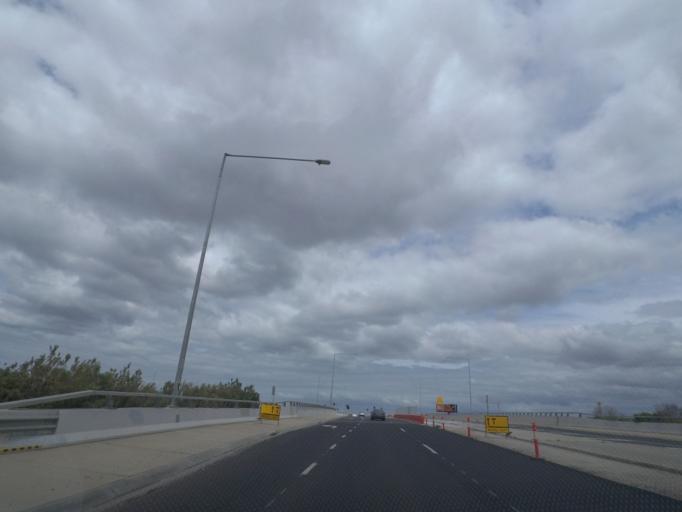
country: AU
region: Victoria
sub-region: Wyndham
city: Williams Landing
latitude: -37.8688
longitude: 144.7481
